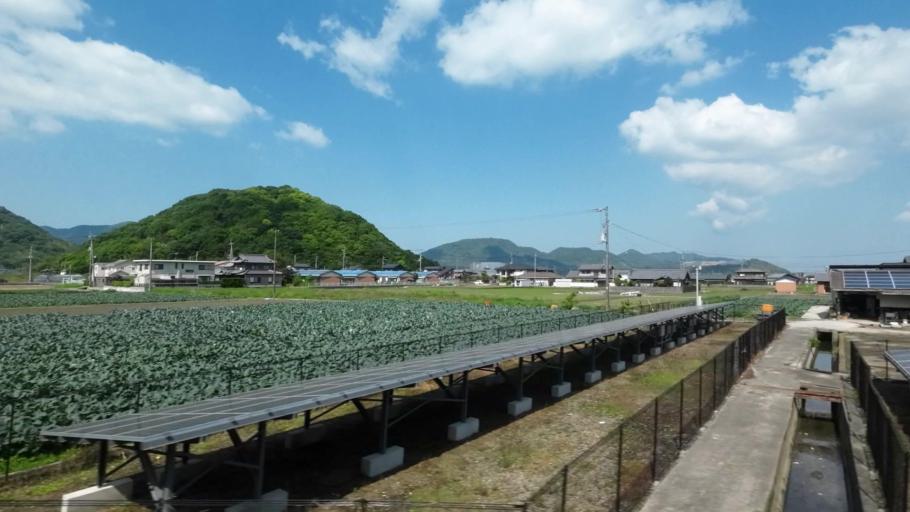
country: JP
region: Kagawa
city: Tadotsu
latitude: 34.1968
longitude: 133.7130
